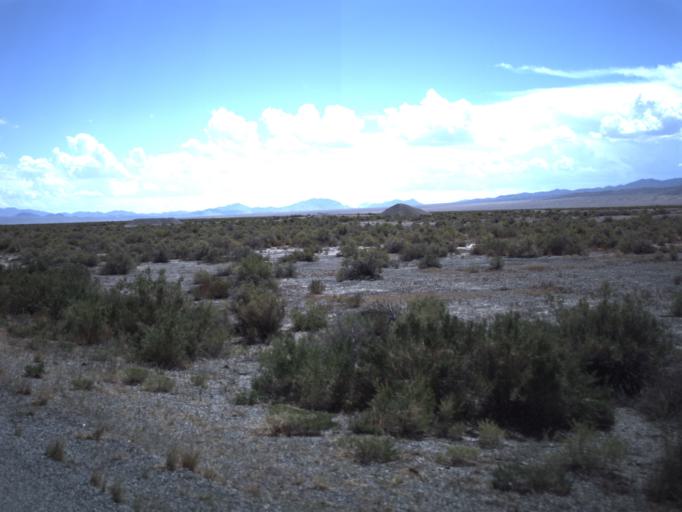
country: US
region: Nevada
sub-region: White Pine County
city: McGill
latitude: 39.0488
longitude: -113.9400
